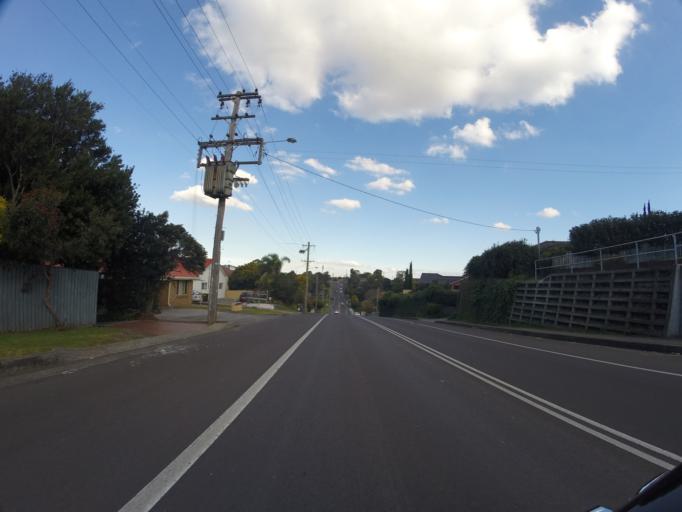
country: AU
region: New South Wales
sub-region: Wollongong
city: Keiraville
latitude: -34.4210
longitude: 150.8691
